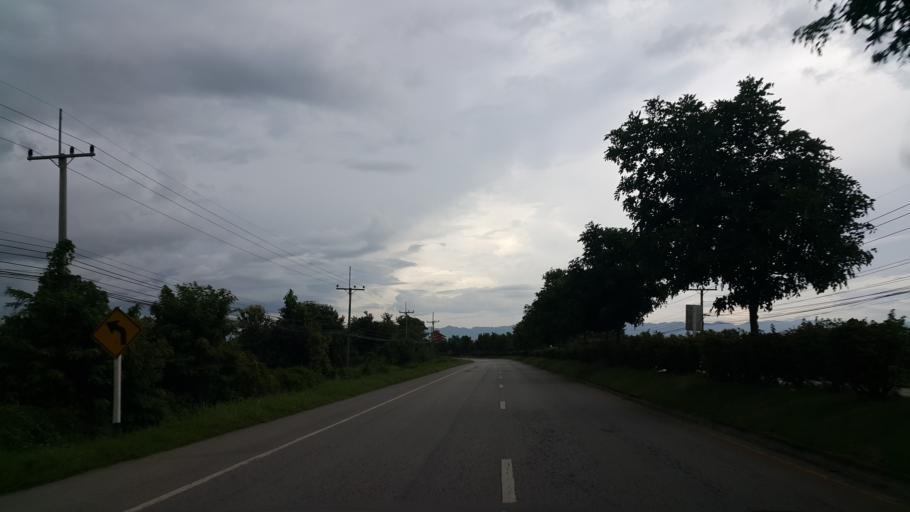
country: TH
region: Phayao
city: Dok Kham Tai
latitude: 19.1559
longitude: 99.9564
